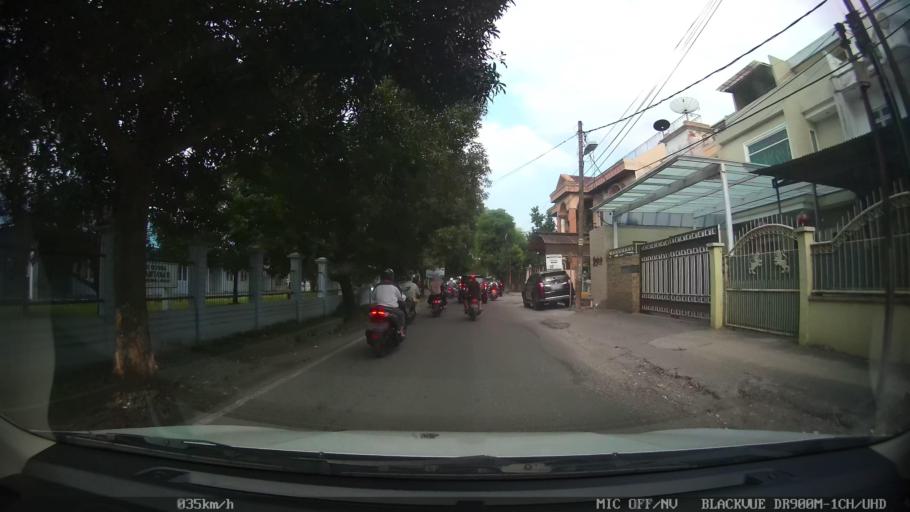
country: ID
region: North Sumatra
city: Medan
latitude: 3.5567
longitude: 98.6809
